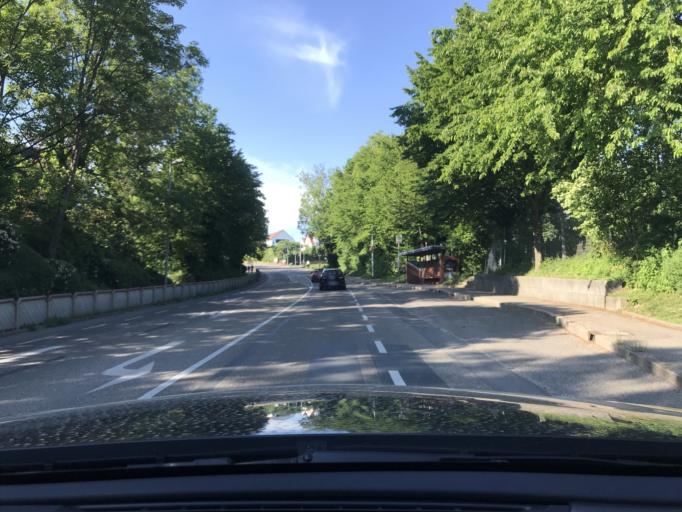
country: DE
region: Baden-Wuerttemberg
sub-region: Regierungsbezirk Stuttgart
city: Waiblingen
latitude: 48.8525
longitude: 9.3266
